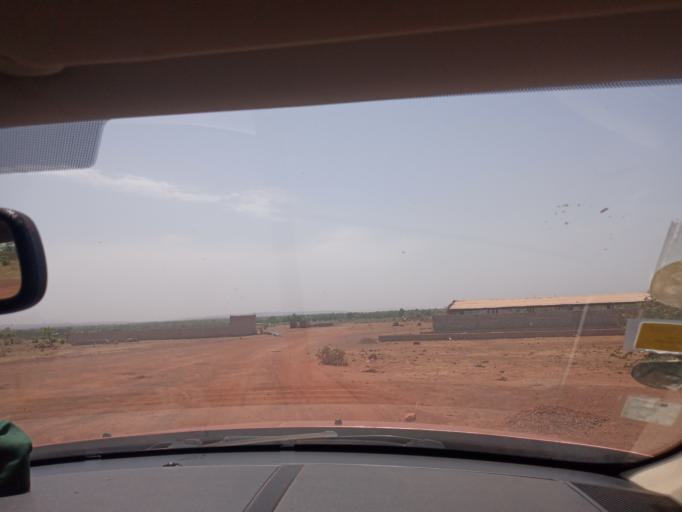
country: ML
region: Bamako
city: Bamako
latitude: 12.5187
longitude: -7.7920
